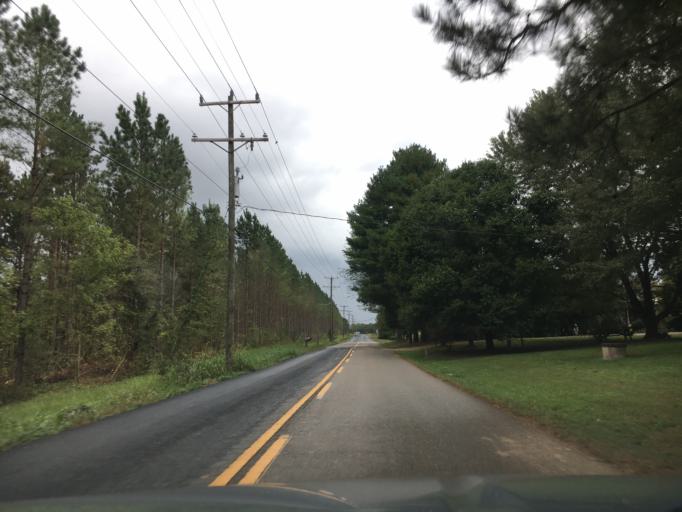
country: US
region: Virginia
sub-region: Amelia County
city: Amelia Court House
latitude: 37.3705
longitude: -77.9772
